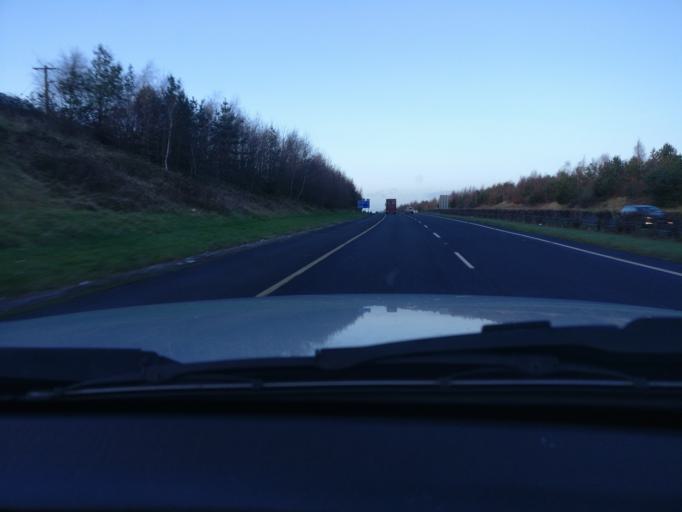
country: IE
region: Leinster
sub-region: Lu
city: Dundalk
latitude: 53.9785
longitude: -6.4268
